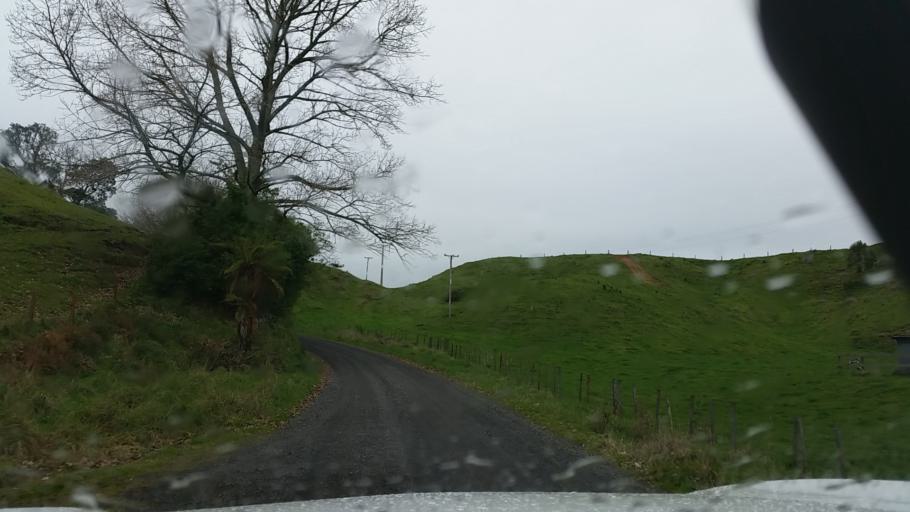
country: NZ
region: Bay of Plenty
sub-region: Rotorua District
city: Rotorua
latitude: -37.9845
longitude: 176.3965
